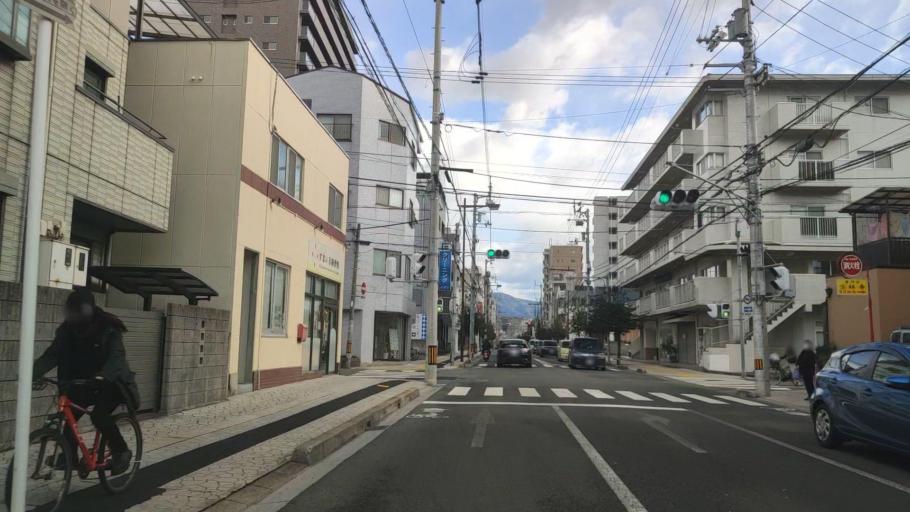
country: JP
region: Ehime
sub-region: Shikoku-chuo Shi
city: Matsuyama
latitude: 33.8527
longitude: 132.7602
